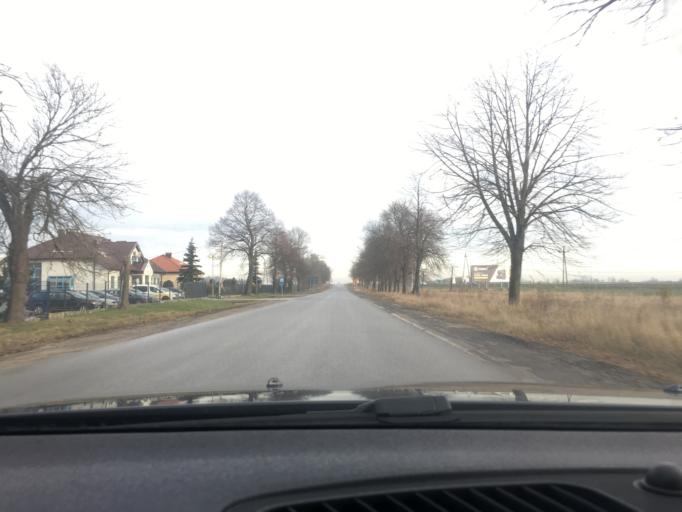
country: PL
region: Swietokrzyskie
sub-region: Powiat jedrzejowski
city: Jedrzejow
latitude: 50.6513
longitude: 20.3197
